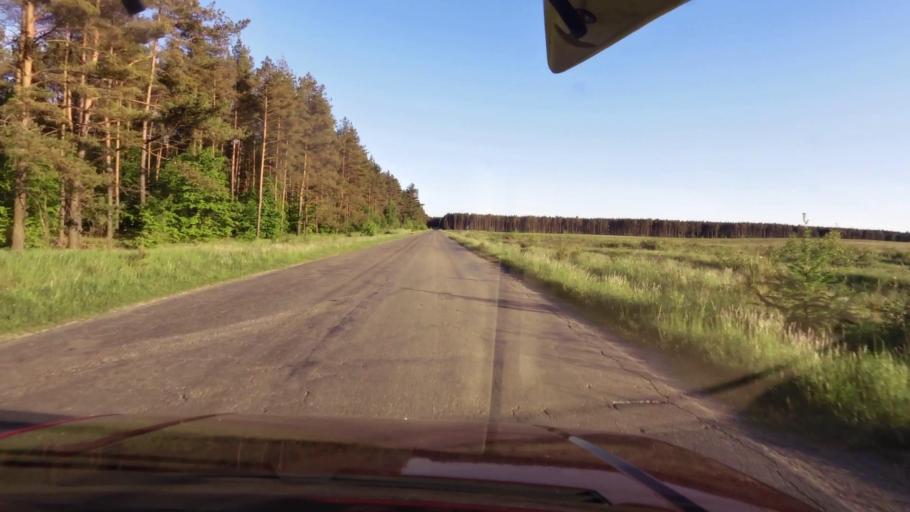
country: PL
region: West Pomeranian Voivodeship
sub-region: Powiat szczecinecki
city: Bialy Bor
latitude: 53.9079
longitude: 16.8107
